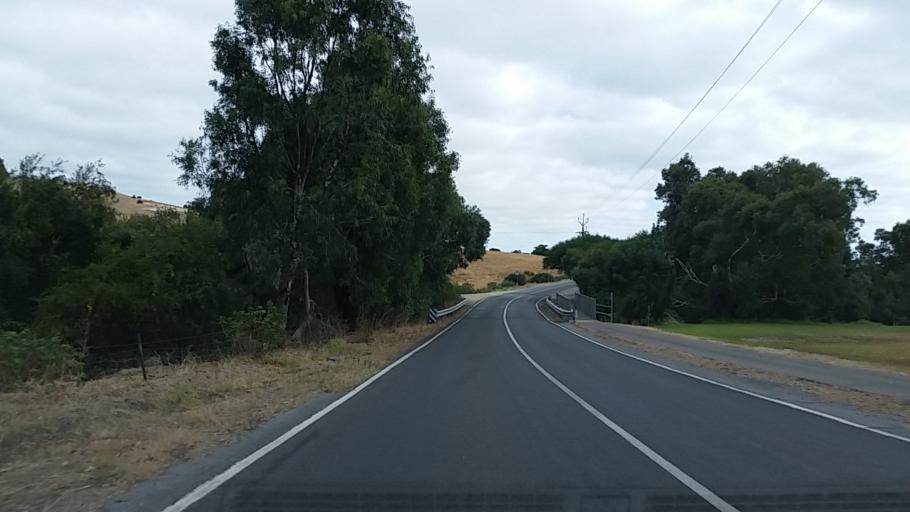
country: AU
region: South Australia
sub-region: Yankalilla
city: Normanville
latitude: -35.4315
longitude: 138.3250
